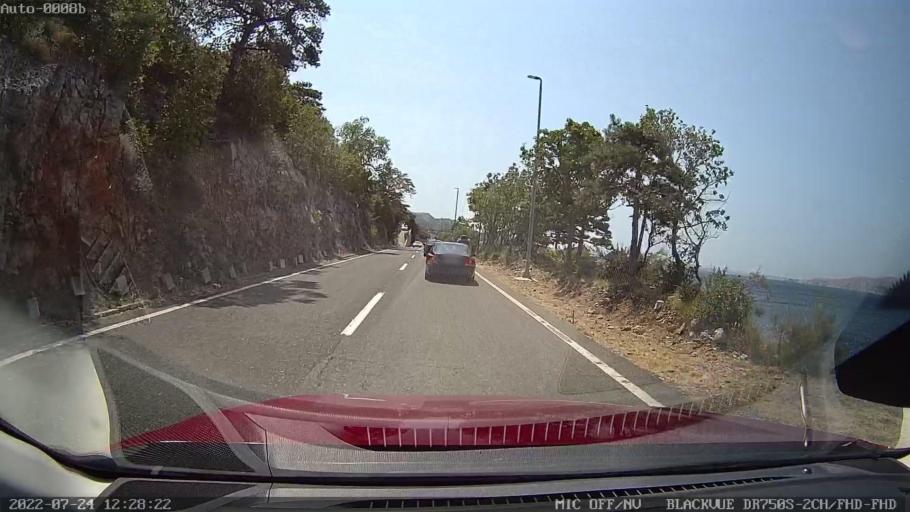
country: HR
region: Licko-Senjska
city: Senj
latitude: 44.9378
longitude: 14.9219
